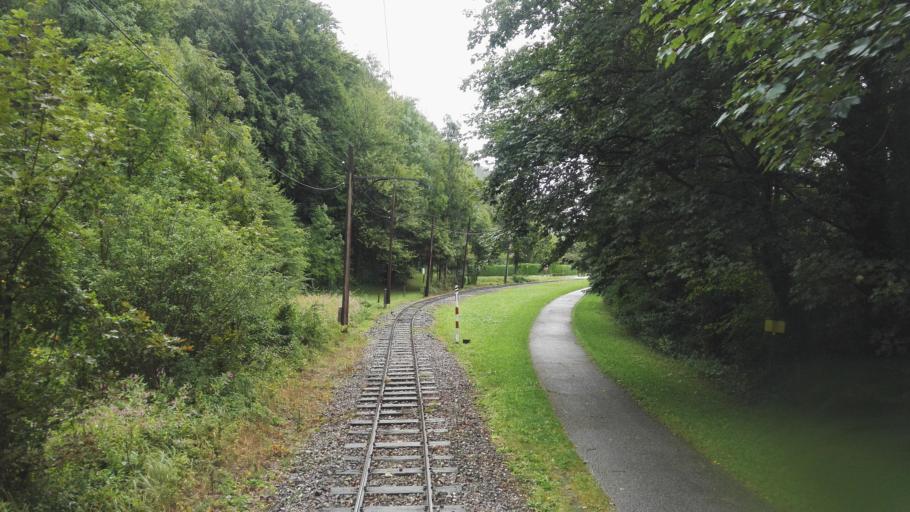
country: AT
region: Lower Austria
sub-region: Politischer Bezirk Neunkirchen
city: Reichenau an der Rax
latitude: 47.7034
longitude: 15.8296
